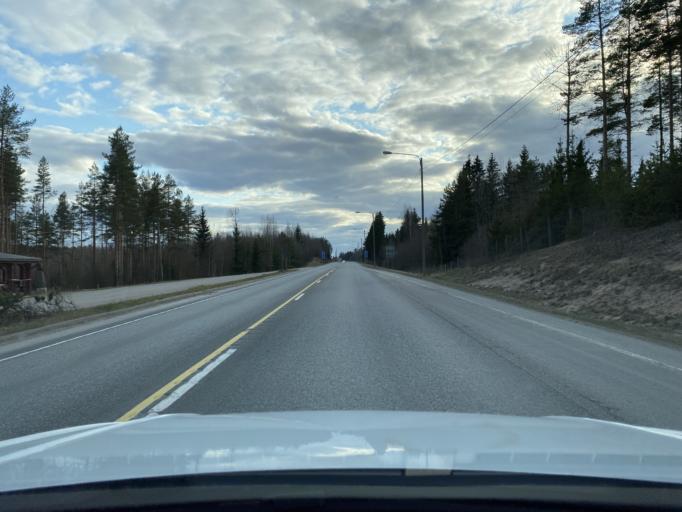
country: FI
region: Haeme
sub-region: Riihimaeki
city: Loppi
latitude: 60.7275
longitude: 24.5196
